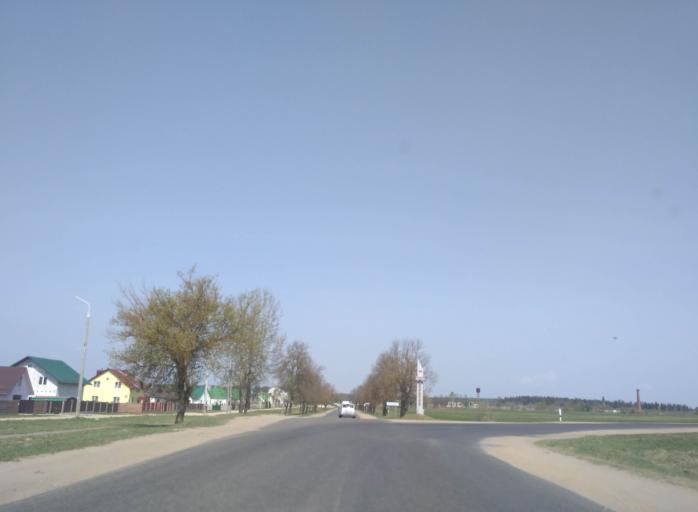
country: BY
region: Minsk
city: Horad Barysaw
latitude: 54.2738
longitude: 28.4967
